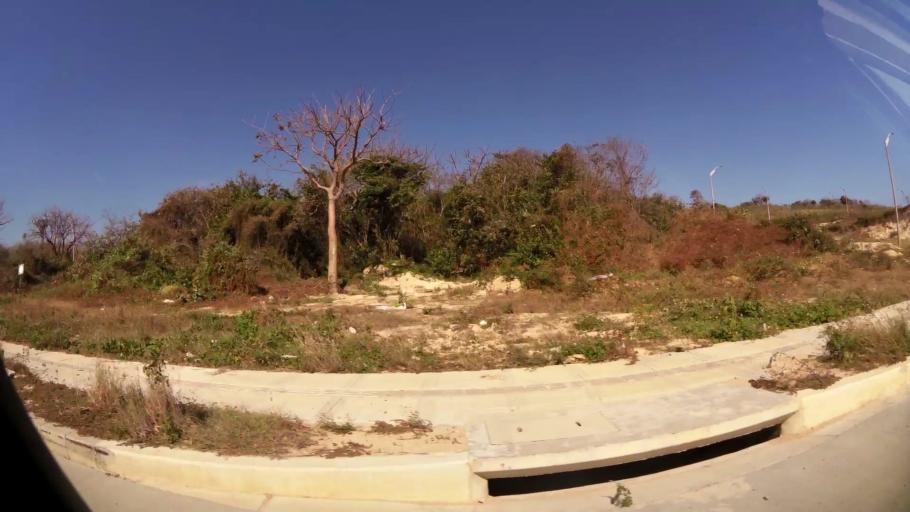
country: CO
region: Atlantico
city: Barranquilla
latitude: 11.0204
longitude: -74.8262
